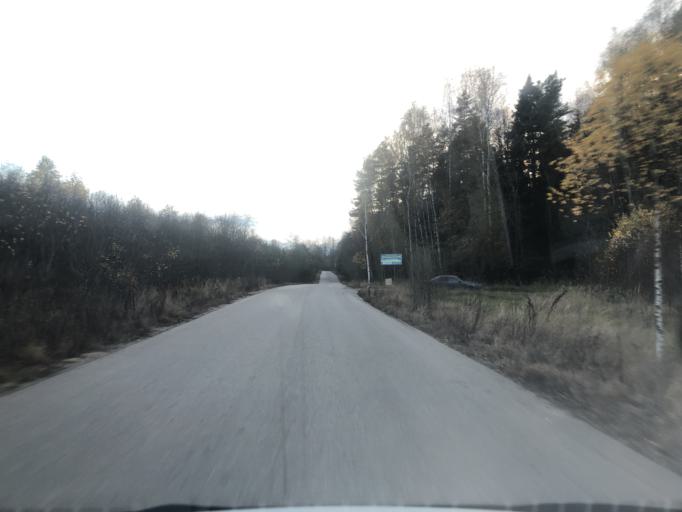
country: RU
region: Moskovskaya
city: Fryanovo
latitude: 56.1566
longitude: 38.3941
